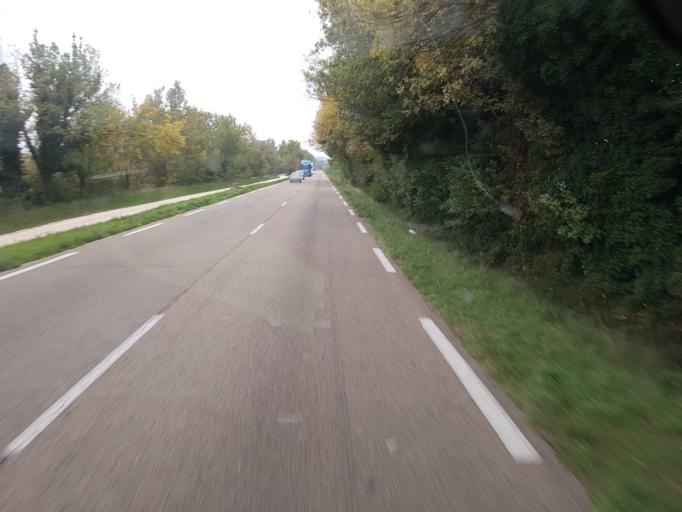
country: FR
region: Provence-Alpes-Cote d'Azur
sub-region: Departement des Bouches-du-Rhone
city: Barbentane
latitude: 43.9192
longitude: 4.7293
